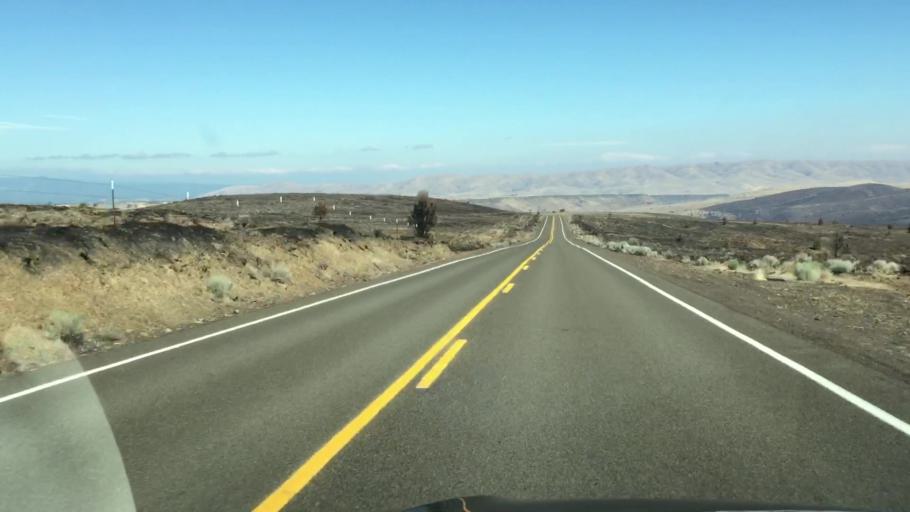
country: US
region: Oregon
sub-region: Jefferson County
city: Warm Springs
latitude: 45.1295
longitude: -121.0484
